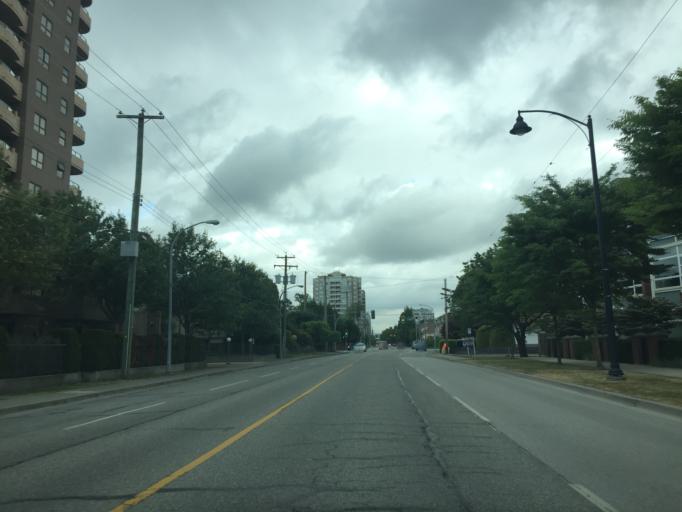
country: CA
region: British Columbia
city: Richmond
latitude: 49.1653
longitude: -123.1315
